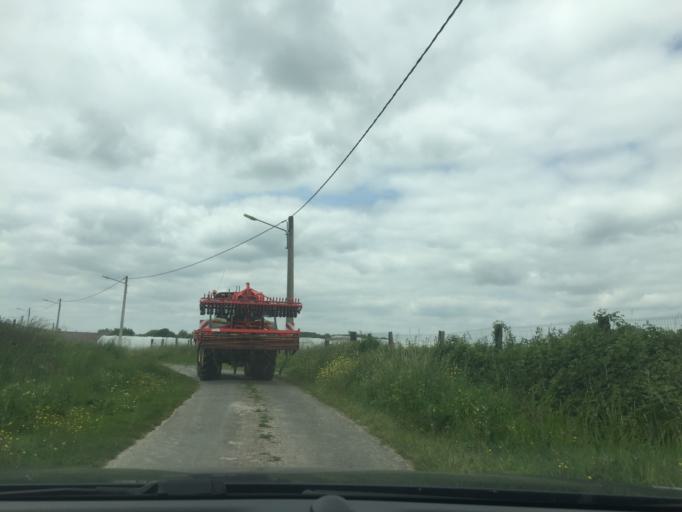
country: BE
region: Wallonia
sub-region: Province du Hainaut
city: Pecq
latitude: 50.6734
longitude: 3.3988
